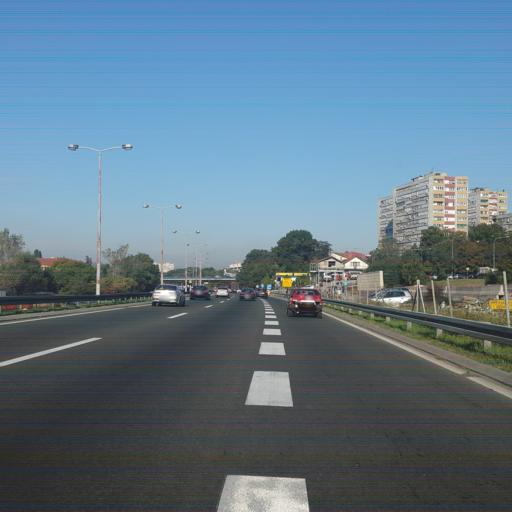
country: RS
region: Central Serbia
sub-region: Belgrade
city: Zvezdara
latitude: 44.7795
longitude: 20.5070
